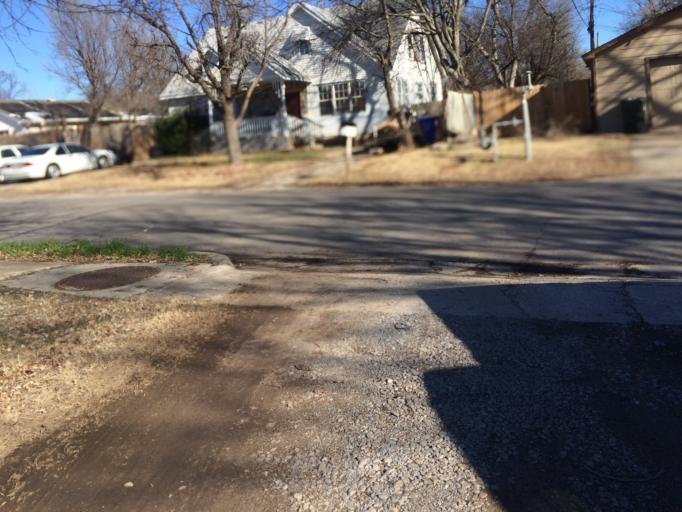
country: US
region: Oklahoma
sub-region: Cleveland County
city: Norman
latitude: 35.2225
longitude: -97.4326
